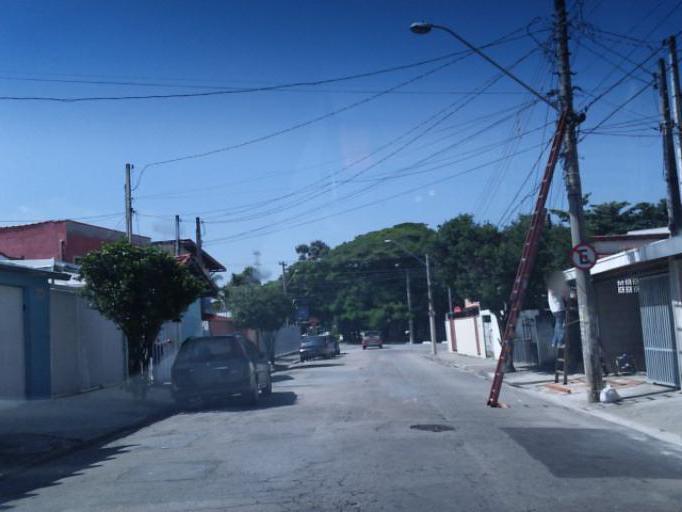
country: BR
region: Sao Paulo
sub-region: Sao Jose Dos Campos
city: Sao Jose dos Campos
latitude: -23.1925
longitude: -45.8796
